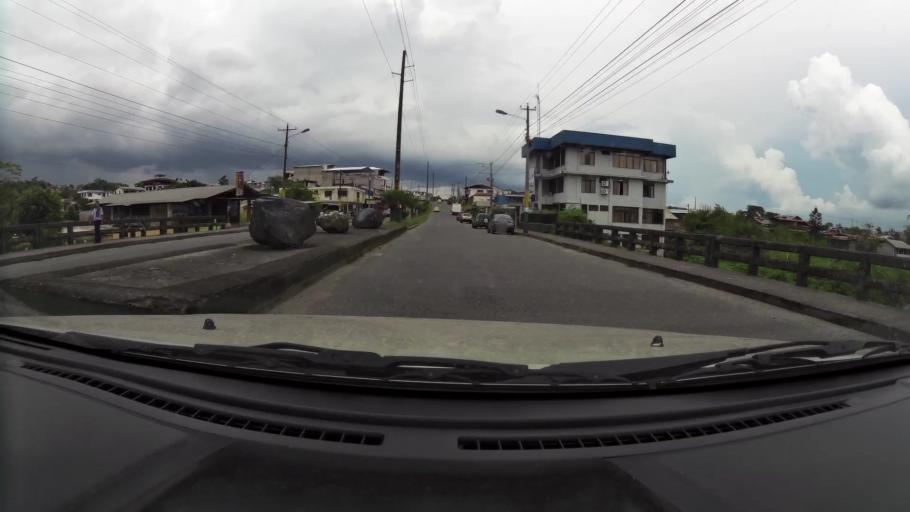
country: EC
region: Pastaza
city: Puyo
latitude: -1.4910
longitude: -78.0095
